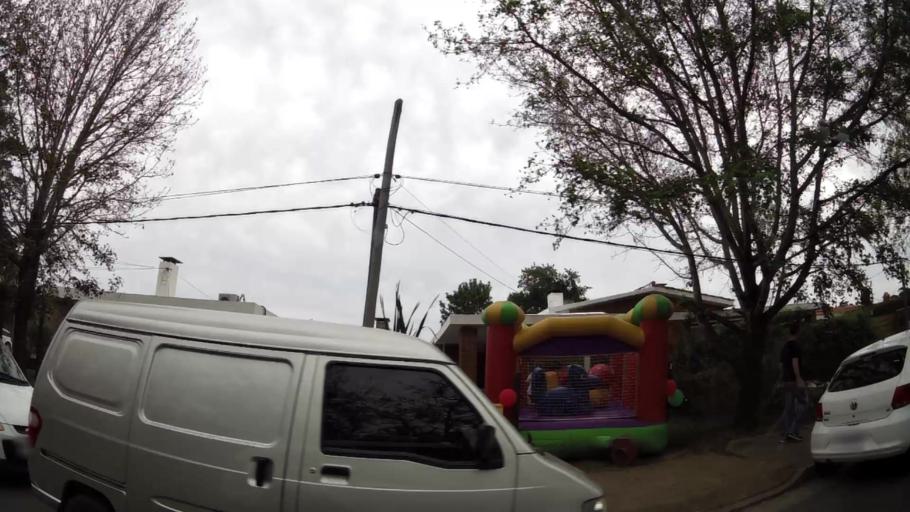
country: UY
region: Maldonado
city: Maldonado
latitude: -34.9119
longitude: -54.9688
